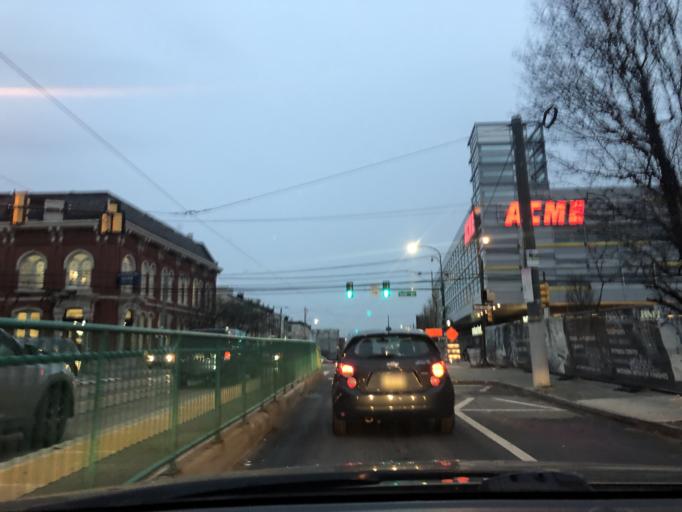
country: US
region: Pennsylvania
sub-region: Philadelphia County
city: Philadelphia
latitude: 39.9695
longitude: -75.1400
